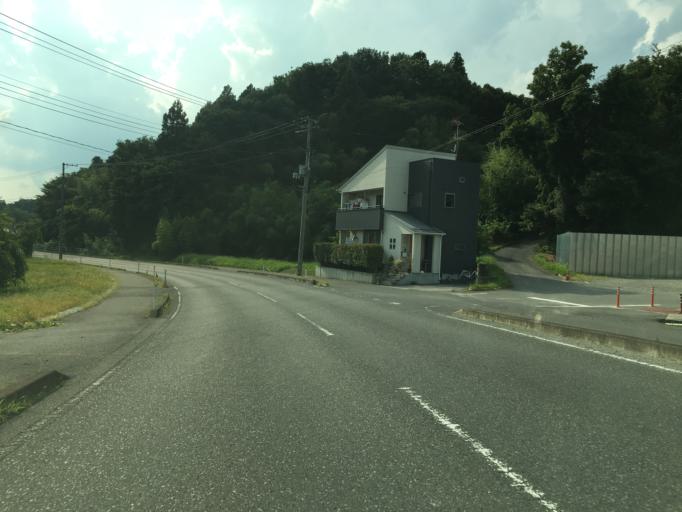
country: JP
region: Fukushima
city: Miharu
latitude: 37.4472
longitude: 140.4313
